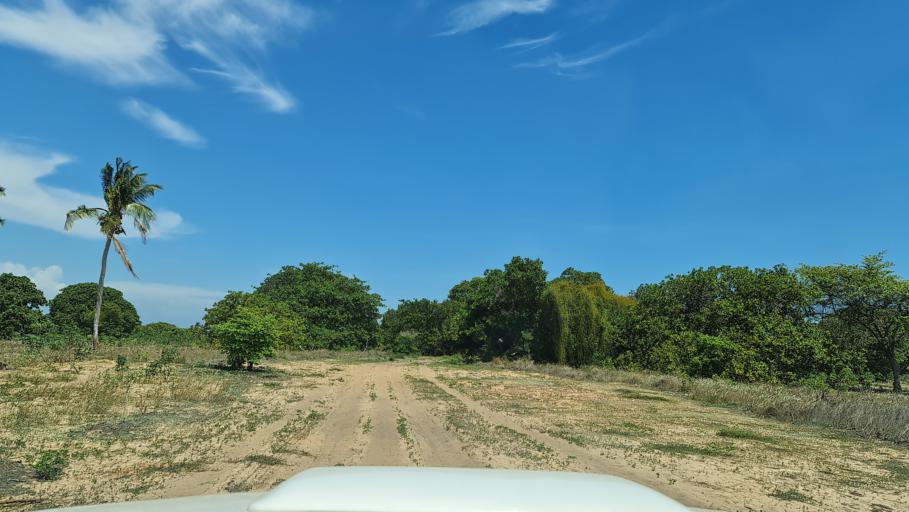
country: MZ
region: Nampula
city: Ilha de Mocambique
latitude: -15.1975
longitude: 40.6045
